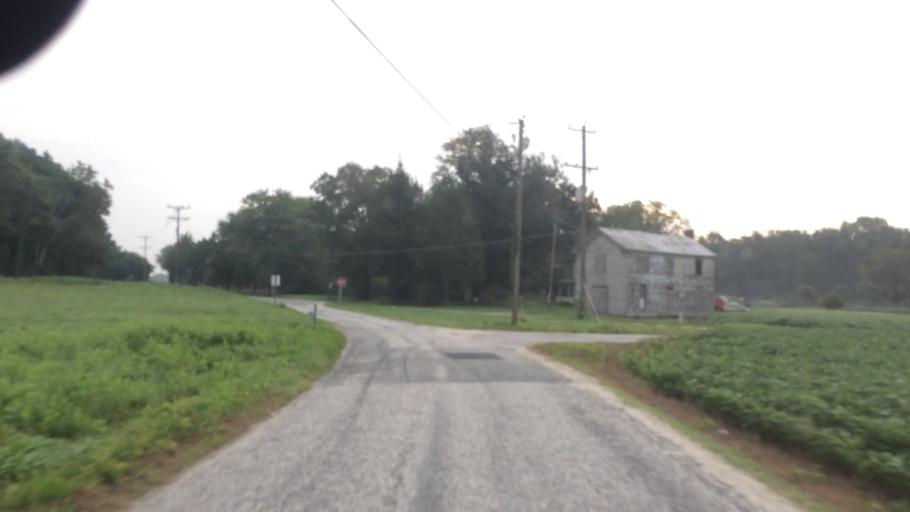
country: US
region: Virginia
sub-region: King William County
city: West Point
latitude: 37.5519
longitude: -76.7325
